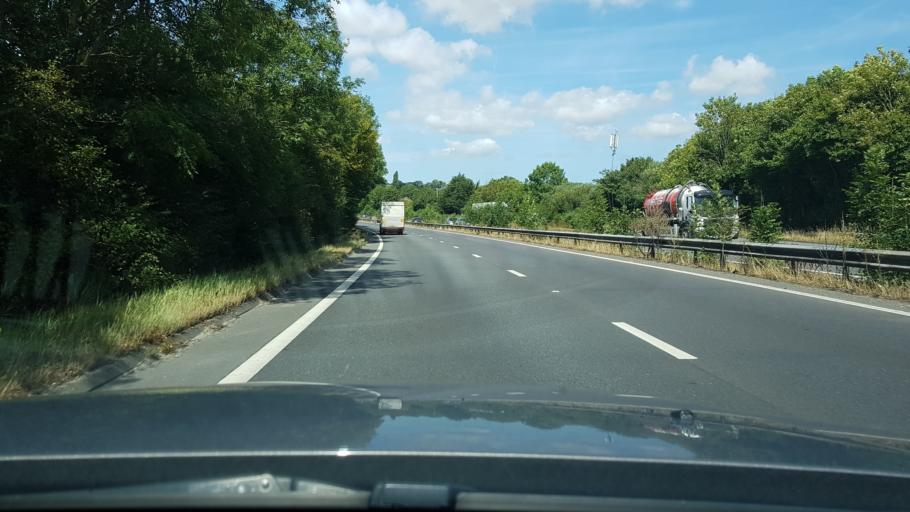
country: GB
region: England
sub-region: West Sussex
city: Chichester
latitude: 50.8403
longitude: -0.8077
